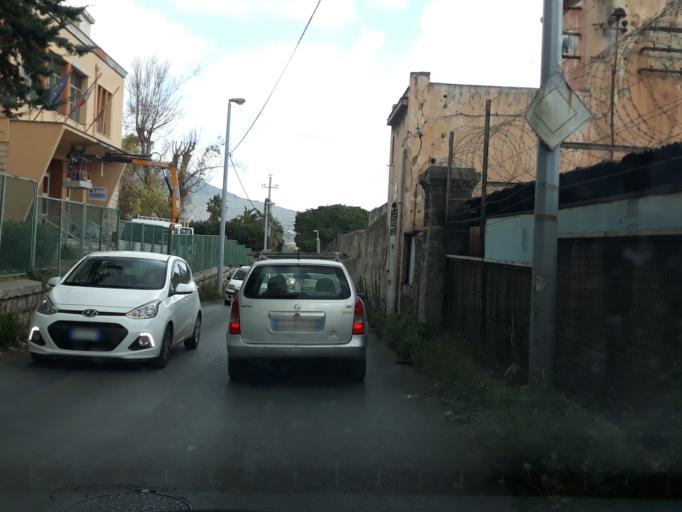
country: IT
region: Sicily
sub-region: Palermo
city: Palermo
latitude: 38.1099
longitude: 13.3088
